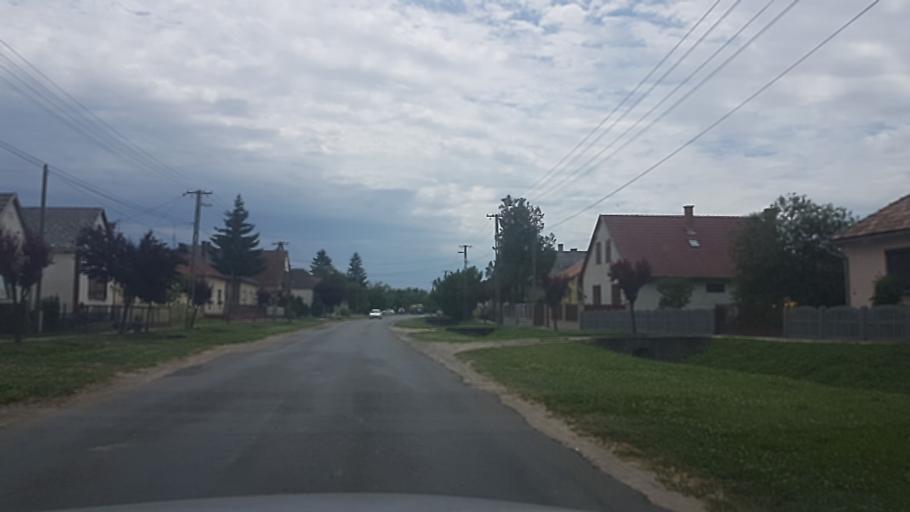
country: HU
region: Somogy
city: Barcs
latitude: 45.9757
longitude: 17.5893
